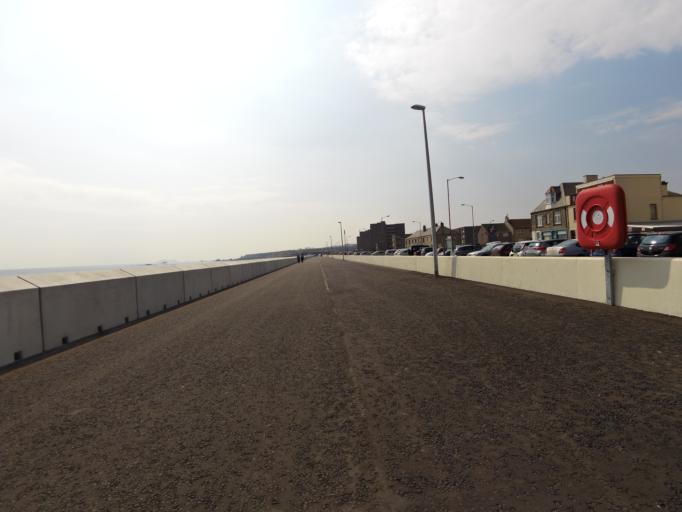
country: GB
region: Scotland
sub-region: Fife
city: Kirkcaldy
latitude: 56.1043
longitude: -3.1584
